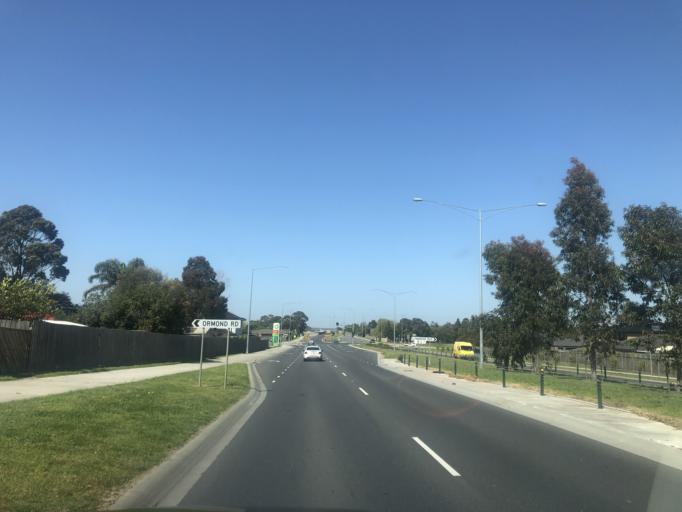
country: AU
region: Victoria
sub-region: Casey
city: Lynbrook
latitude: -38.0457
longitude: 145.2654
